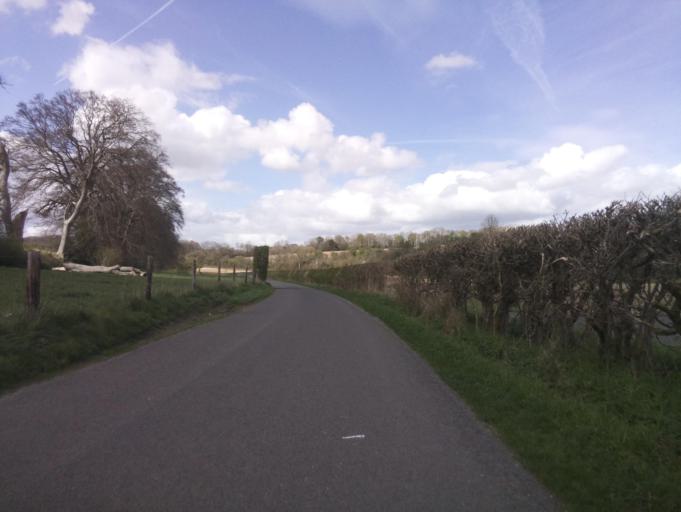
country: GB
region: England
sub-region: West Berkshire
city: Kintbury
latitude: 51.3227
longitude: -1.4635
